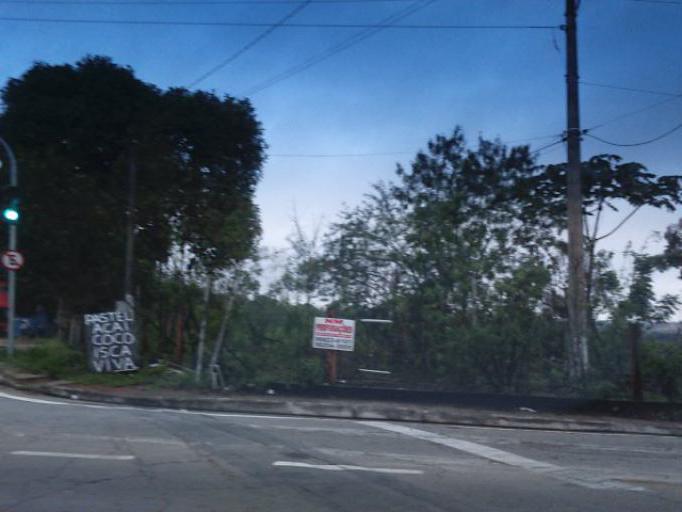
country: BR
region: Sao Paulo
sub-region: Sao Jose Dos Campos
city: Sao Jose dos Campos
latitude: -23.2286
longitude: -45.8719
